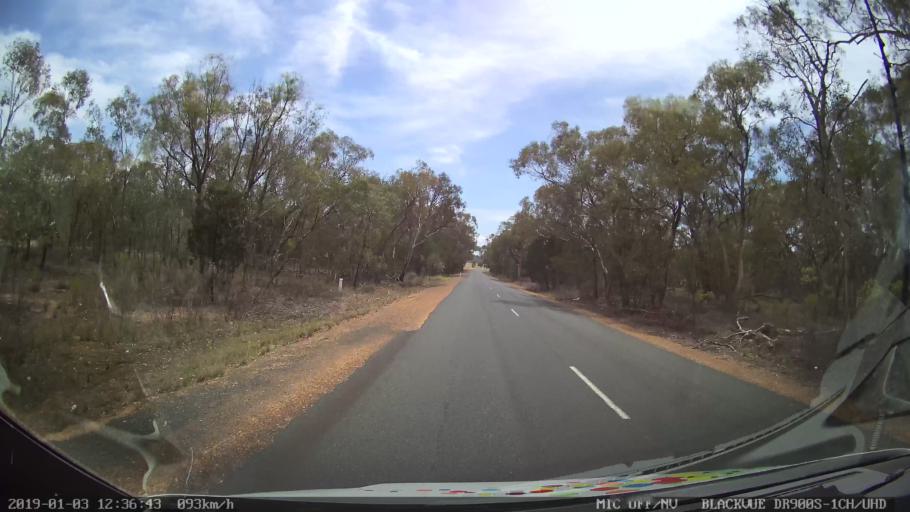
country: AU
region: New South Wales
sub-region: Weddin
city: Grenfell
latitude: -33.8512
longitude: 148.1783
